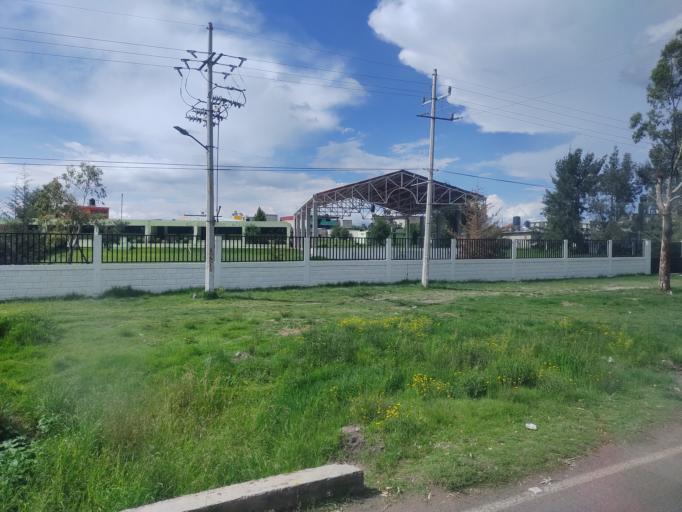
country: MX
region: Mexico
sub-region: Aculco
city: El Colorado
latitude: 20.0960
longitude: -99.7625
